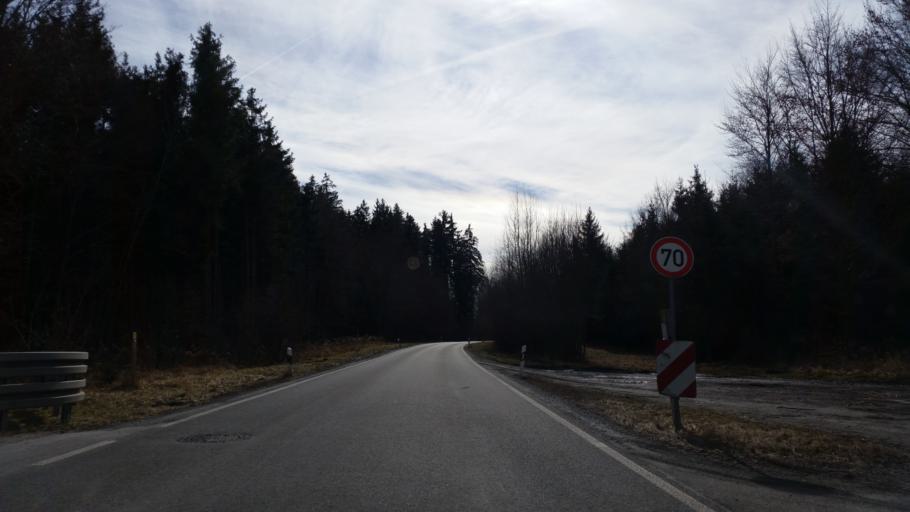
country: DE
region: Bavaria
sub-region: Upper Bavaria
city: Oberpframmern
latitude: 48.0423
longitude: 11.8153
